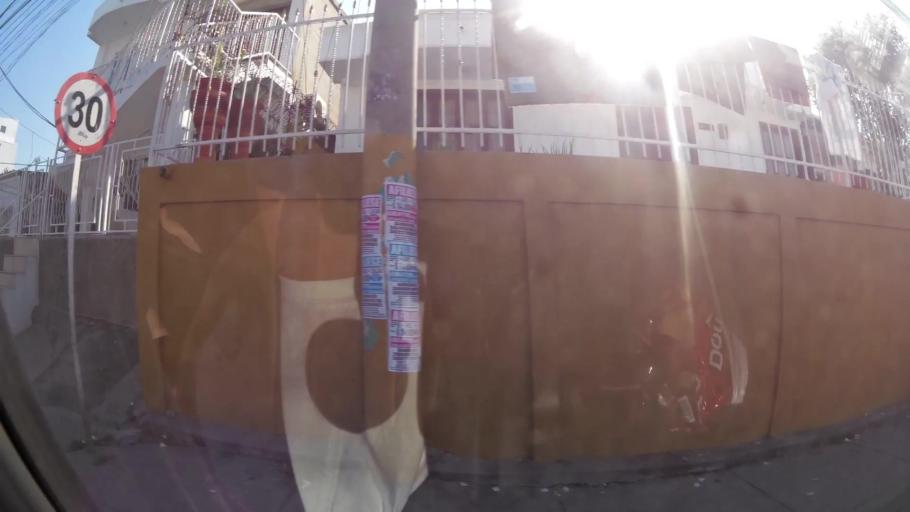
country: CO
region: Bolivar
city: Cartagena
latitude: 10.3976
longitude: -75.4968
